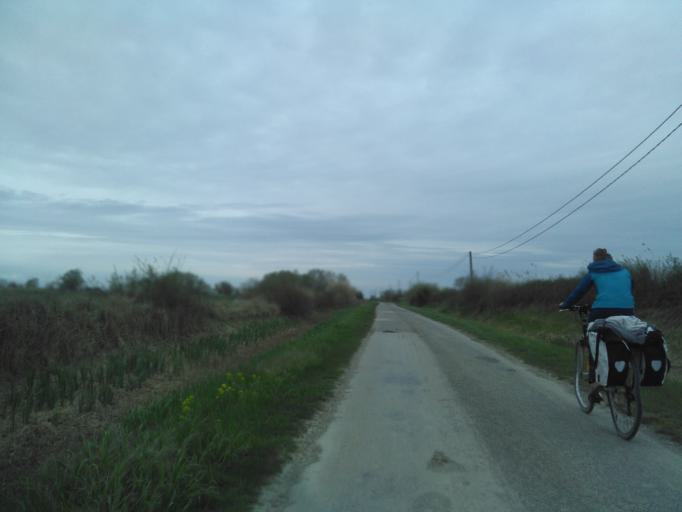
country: FR
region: Provence-Alpes-Cote d'Azur
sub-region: Departement des Bouches-du-Rhone
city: Arles
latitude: 43.5840
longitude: 4.5422
